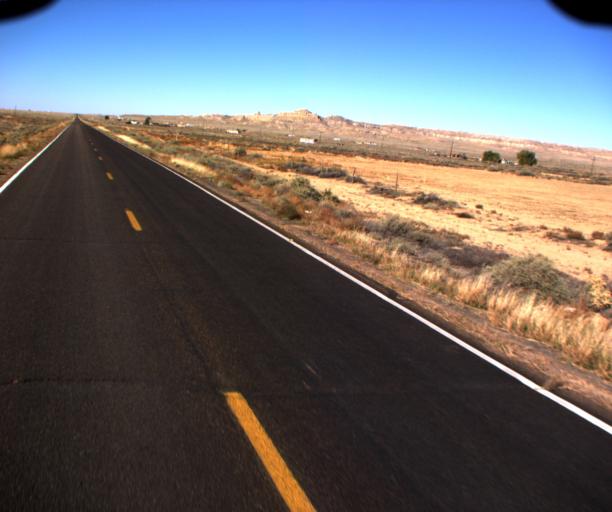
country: US
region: Arizona
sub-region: Navajo County
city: First Mesa
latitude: 35.8011
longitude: -110.4428
